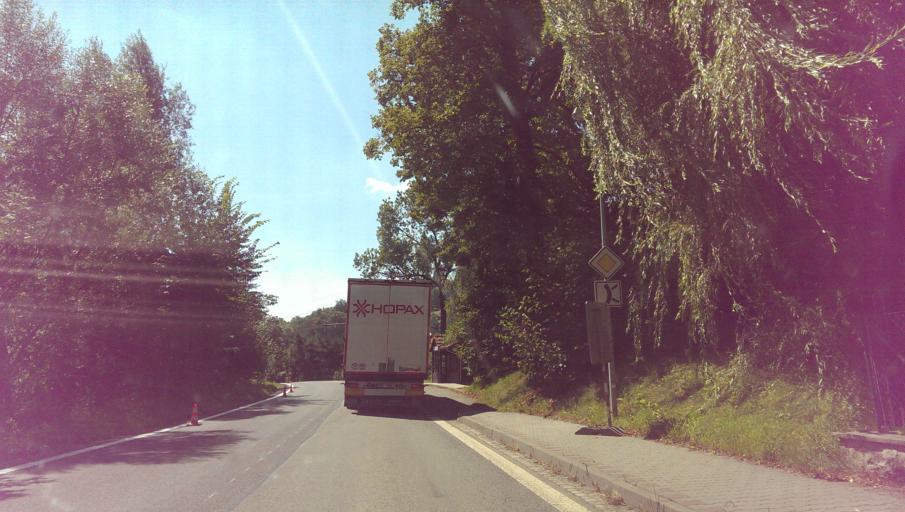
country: CZ
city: Lichnov (o. Novy Jicin)
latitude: 49.5896
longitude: 18.1912
